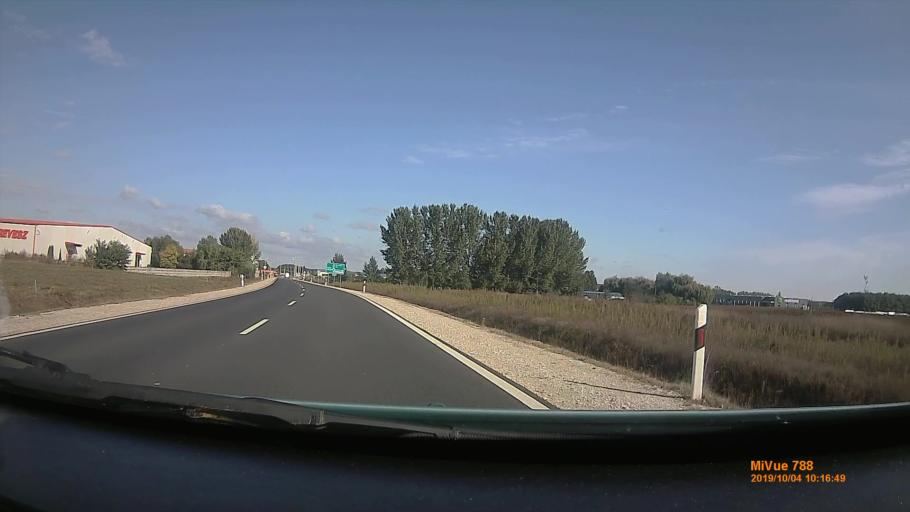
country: HU
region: Szabolcs-Szatmar-Bereg
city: Nyiregyhaza
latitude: 47.9531
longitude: 21.6554
